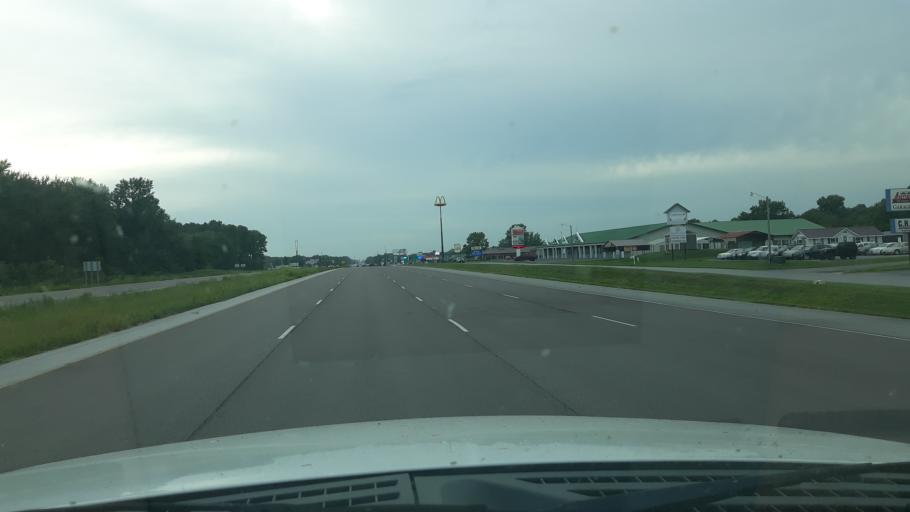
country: US
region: Illinois
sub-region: Williamson County
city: Crainville
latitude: 37.7452
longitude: -89.0696
